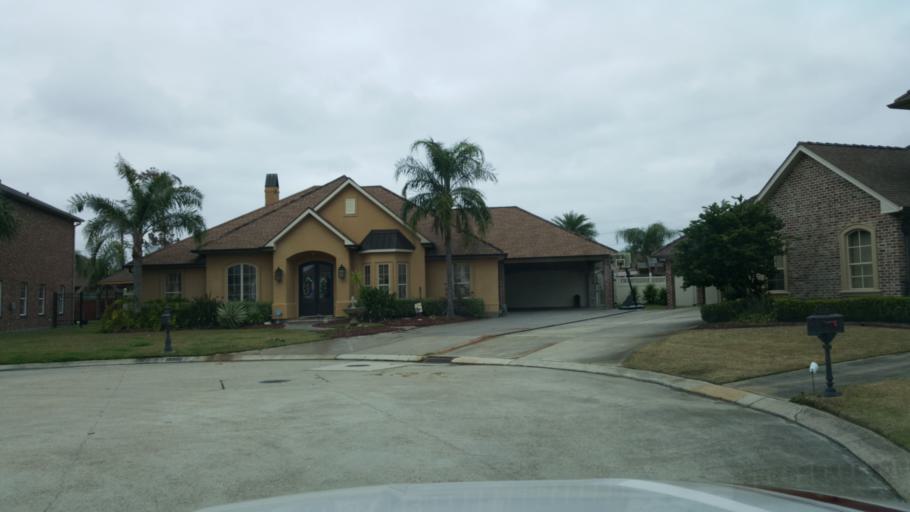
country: US
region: Louisiana
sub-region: Jefferson Parish
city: Woodmere
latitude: 29.8792
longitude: -90.0788
